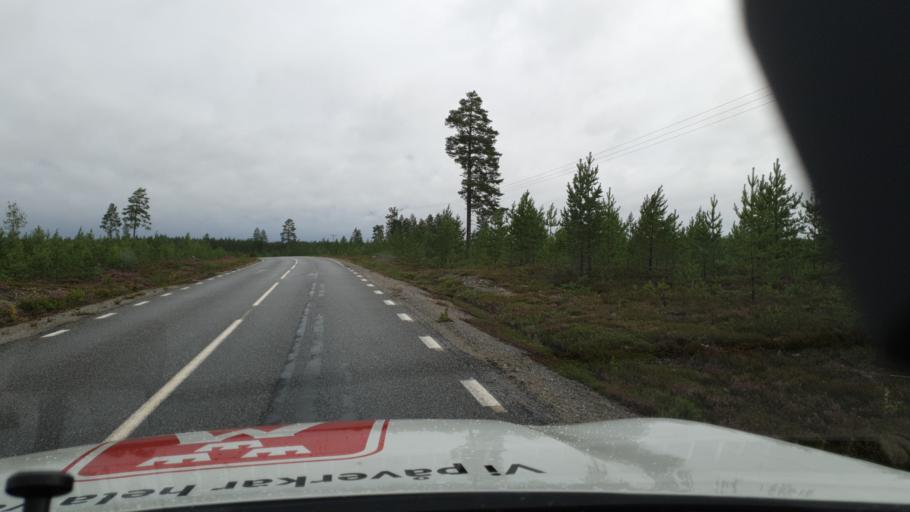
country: SE
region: Vaesterbotten
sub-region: Umea Kommun
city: Saevar
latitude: 63.9692
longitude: 20.5076
